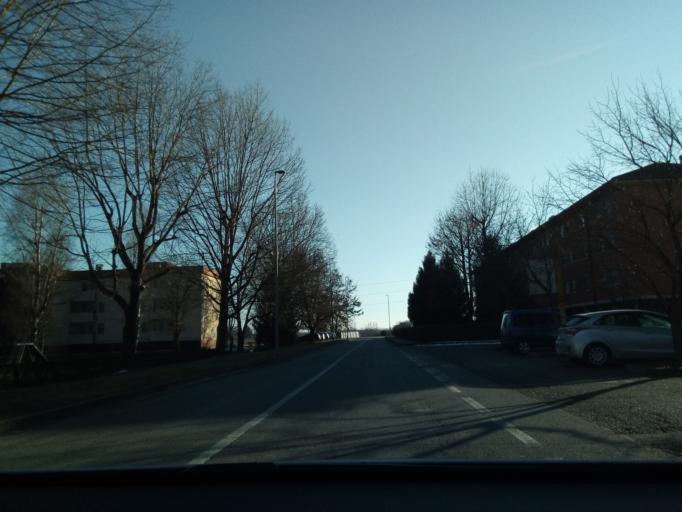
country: IT
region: Piedmont
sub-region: Provincia di Torino
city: Cascinette d'Ivrea
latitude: 45.4611
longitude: 7.9091
